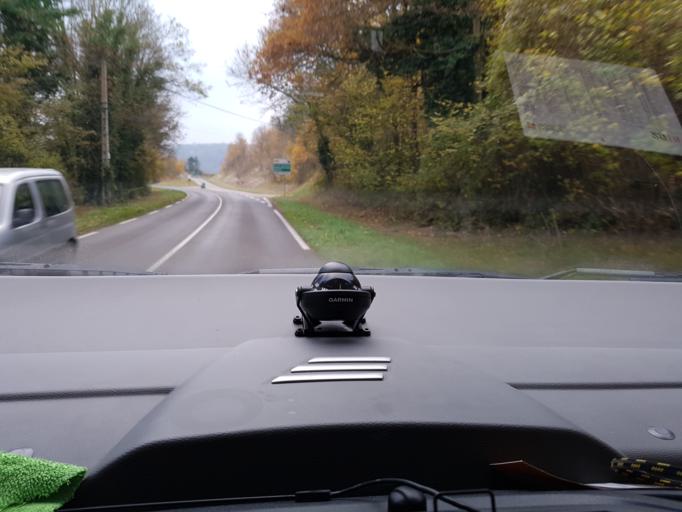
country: FR
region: Haute-Normandie
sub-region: Departement de la Seine-Maritime
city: Eu
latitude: 50.0617
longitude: 1.4210
